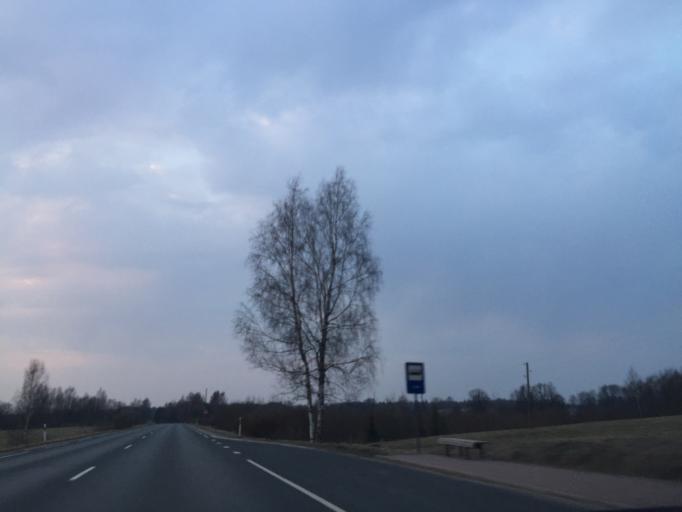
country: LV
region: Raunas
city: Rauna
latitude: 57.2437
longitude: 25.5560
